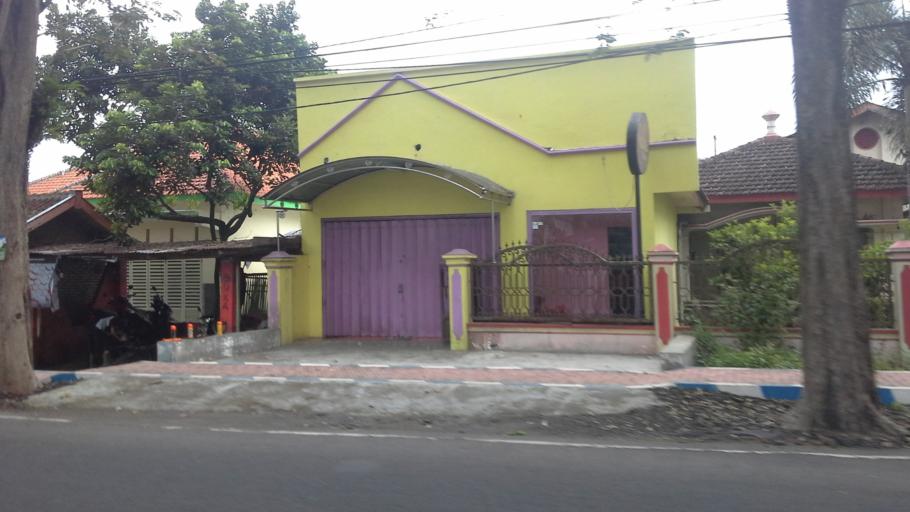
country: ID
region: East Java
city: Bondowoso
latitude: -7.9303
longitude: 113.8167
